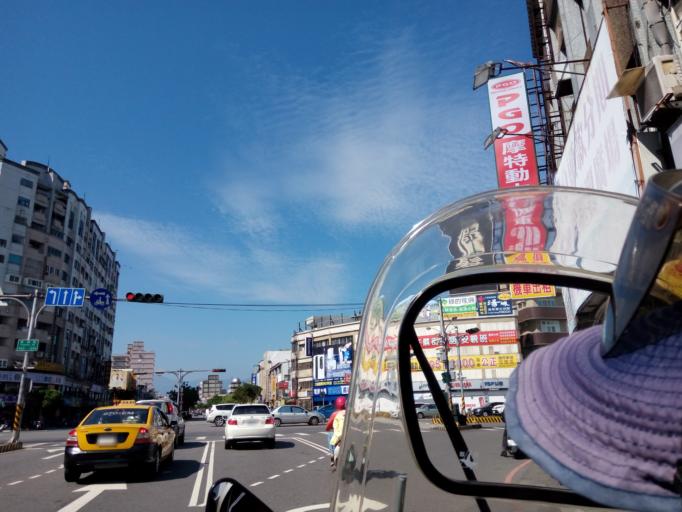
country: TW
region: Taiwan
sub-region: Yilan
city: Yilan
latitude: 24.6800
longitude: 121.7644
